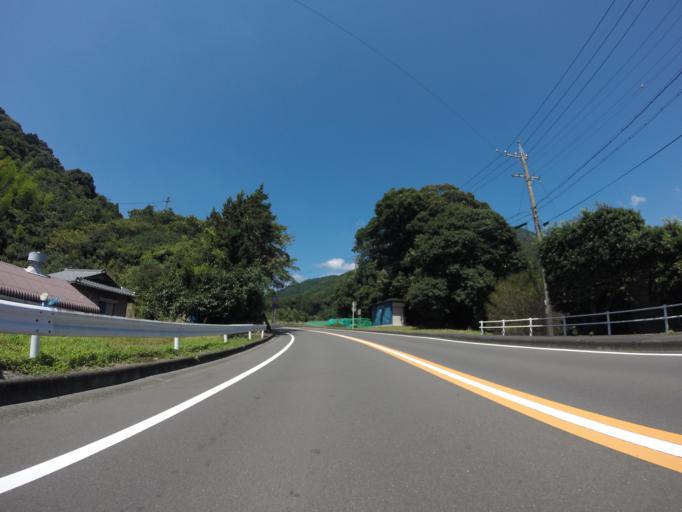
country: JP
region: Shizuoka
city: Shizuoka-shi
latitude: 35.0173
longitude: 138.2678
